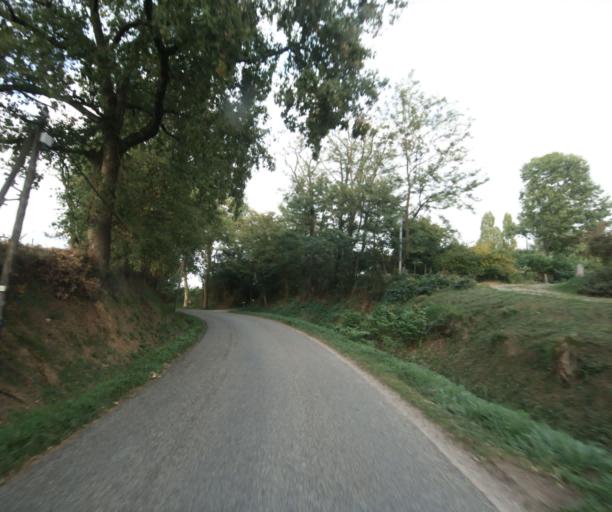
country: FR
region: Aquitaine
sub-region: Departement des Landes
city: Gabarret
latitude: 43.9516
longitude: 0.0898
